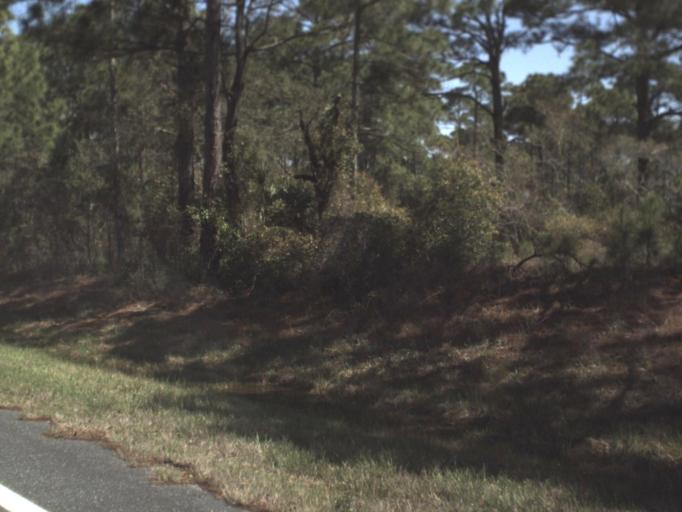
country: US
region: Florida
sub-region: Wakulla County
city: Crawfordville
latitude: 30.0044
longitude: -84.3969
